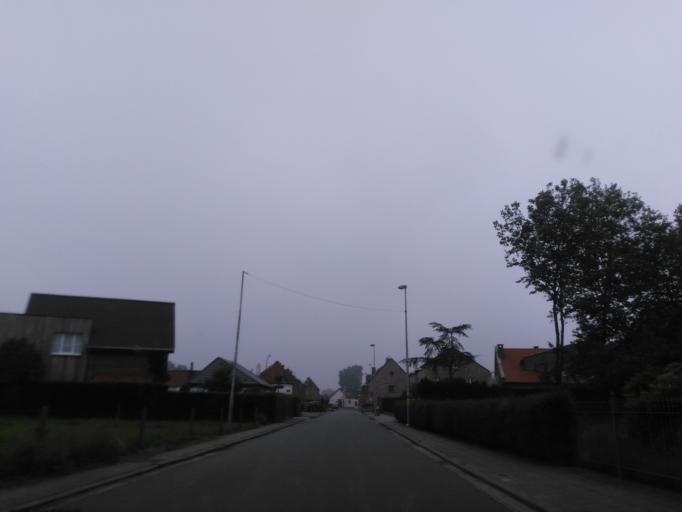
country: BE
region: Flanders
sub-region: Provincie Oost-Vlaanderen
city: Beveren
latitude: 51.2232
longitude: 4.1922
